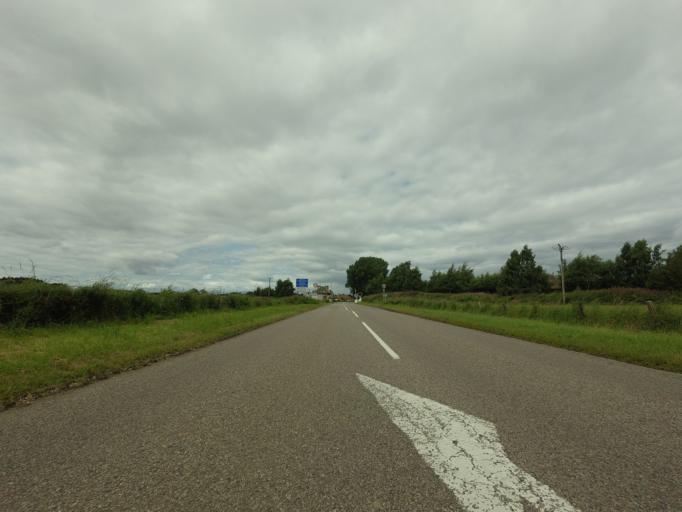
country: GB
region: Scotland
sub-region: Moray
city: Kinloss
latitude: 57.6313
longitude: -3.5573
